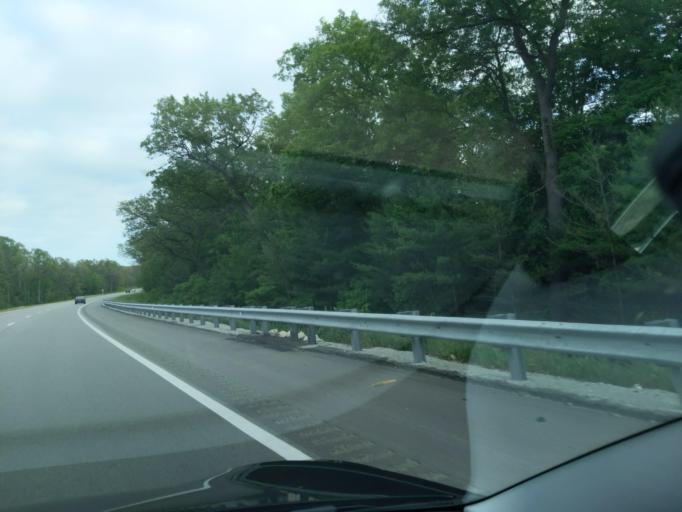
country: US
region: Michigan
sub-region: Muskegon County
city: Lakewood Club
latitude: 43.3156
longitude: -86.2248
